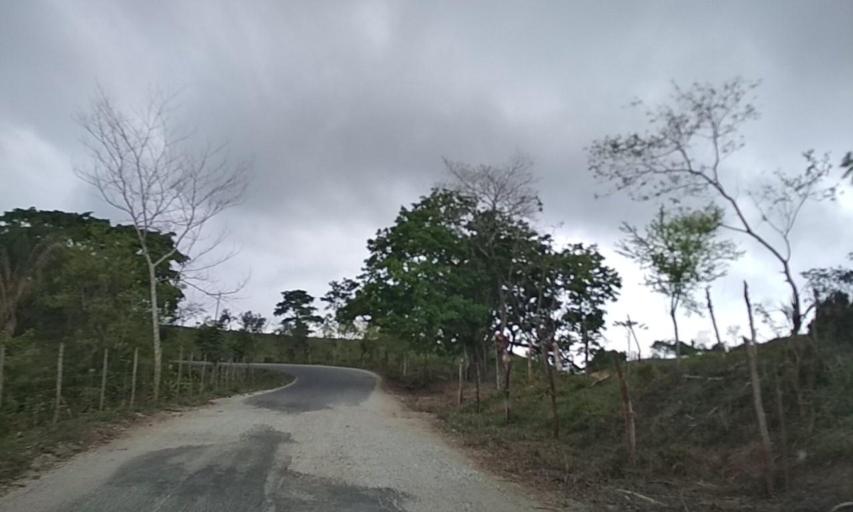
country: MX
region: Tabasco
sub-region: Huimanguillo
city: Francisco Rueda
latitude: 17.6332
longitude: -94.0906
